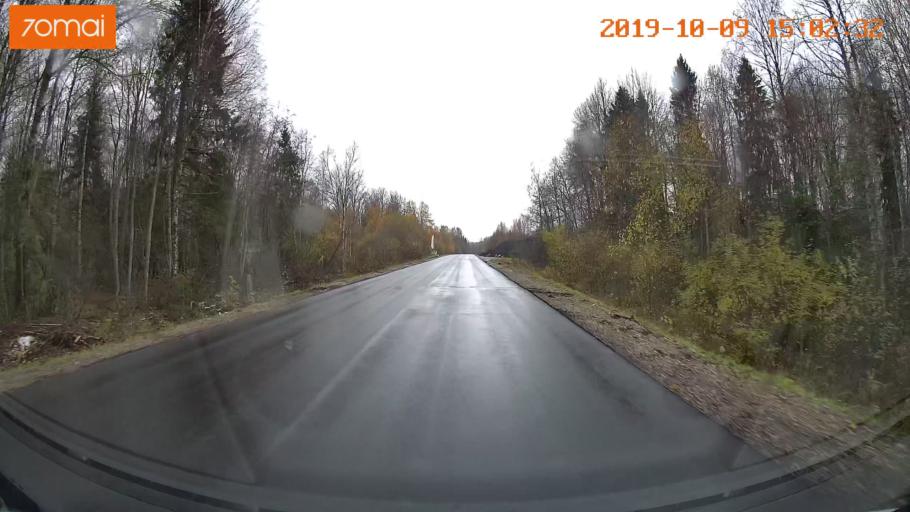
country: RU
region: Kostroma
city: Chistyye Bory
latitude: 58.2836
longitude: 41.6786
